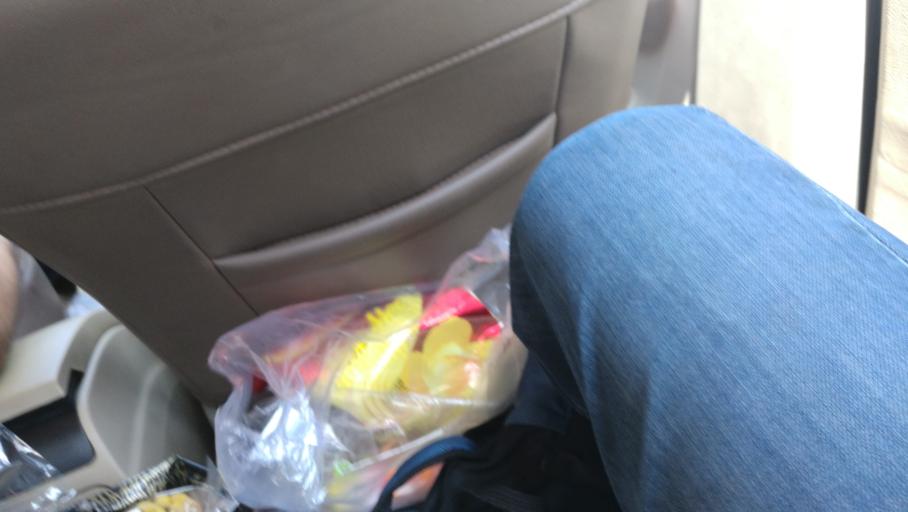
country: IR
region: Alborz
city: Karaj
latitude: 35.9481
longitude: 51.0837
